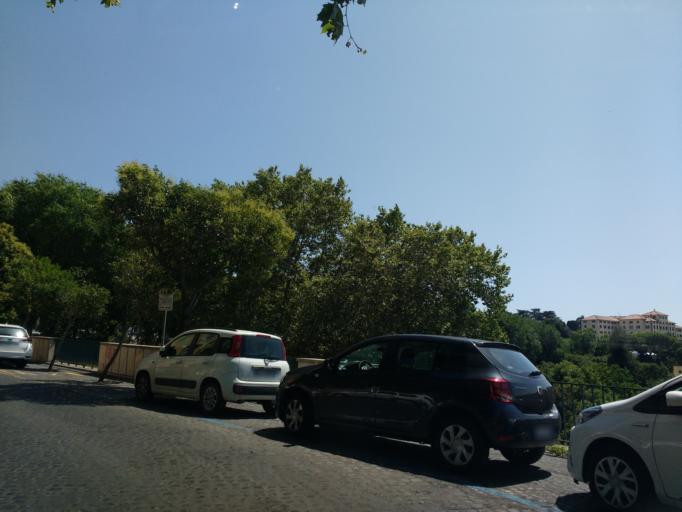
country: IT
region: Latium
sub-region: Citta metropolitana di Roma Capitale
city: Armetta
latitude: 41.8073
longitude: 12.6791
